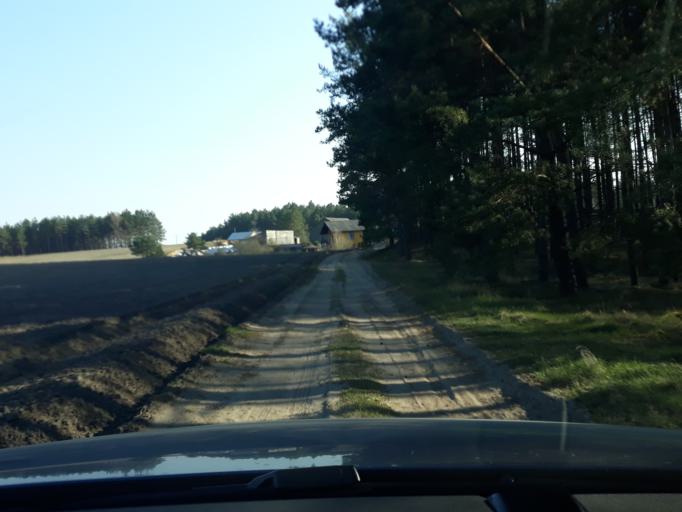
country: PL
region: Pomeranian Voivodeship
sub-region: Powiat bytowski
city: Lipnica
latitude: 53.8937
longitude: 17.4944
